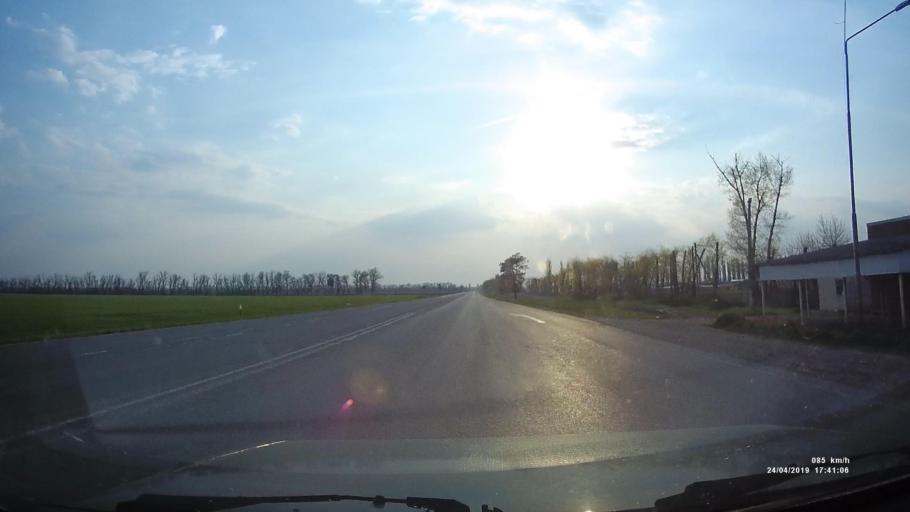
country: RU
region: Rostov
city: Tselina
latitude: 46.5303
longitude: 40.9770
